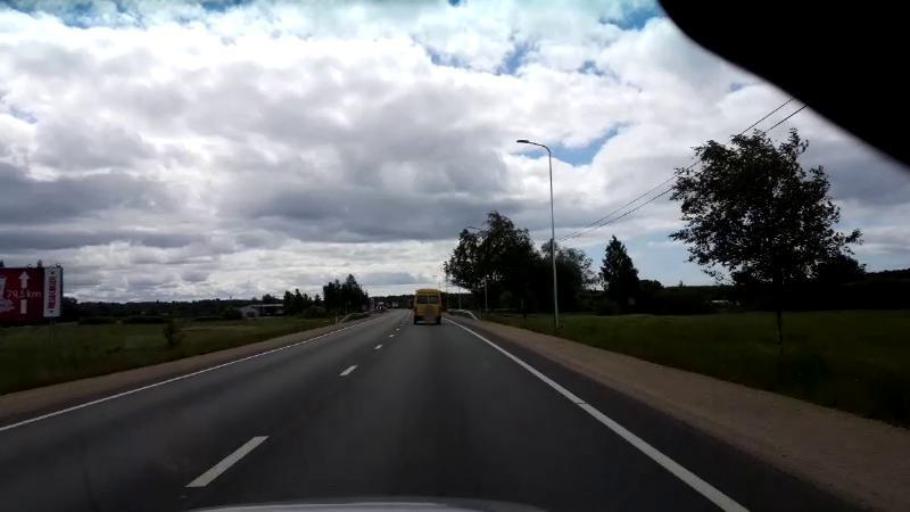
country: LV
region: Salacgrivas
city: Salacgriva
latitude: 57.7433
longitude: 24.3600
